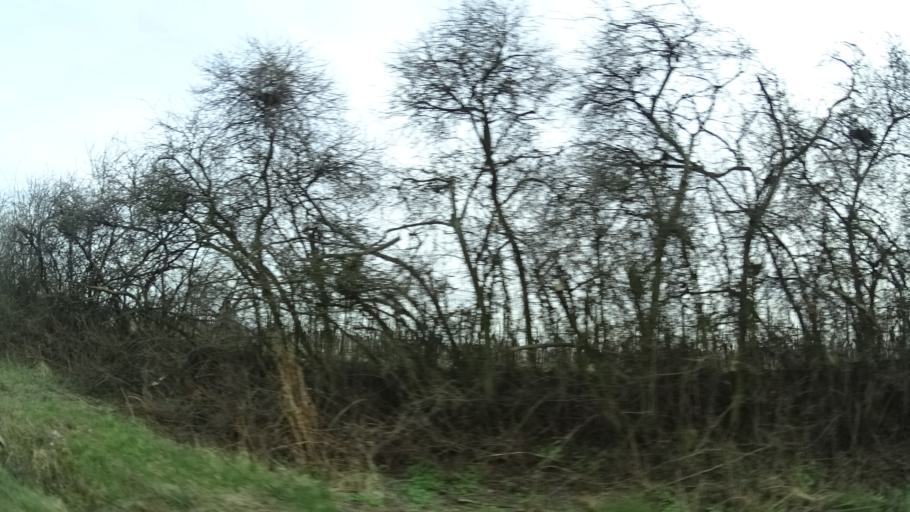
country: DE
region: Rheinland-Pfalz
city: Maikammer
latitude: 49.3153
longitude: 8.1460
